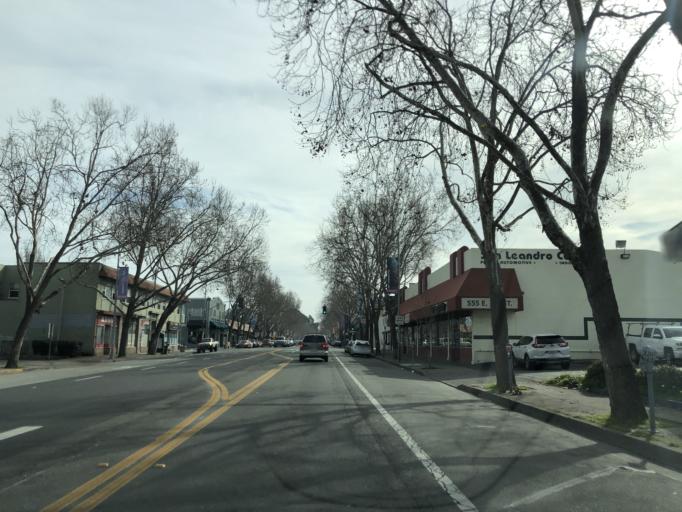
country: US
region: California
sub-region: Alameda County
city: San Leandro
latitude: 37.7315
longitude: -122.1611
